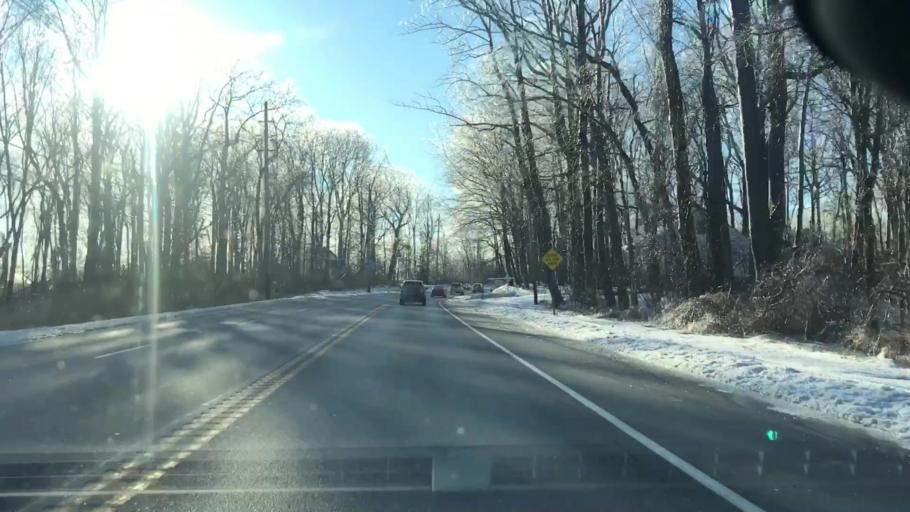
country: US
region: New Jersey
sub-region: Morris County
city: Netcong
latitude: 40.8790
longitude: -74.6934
